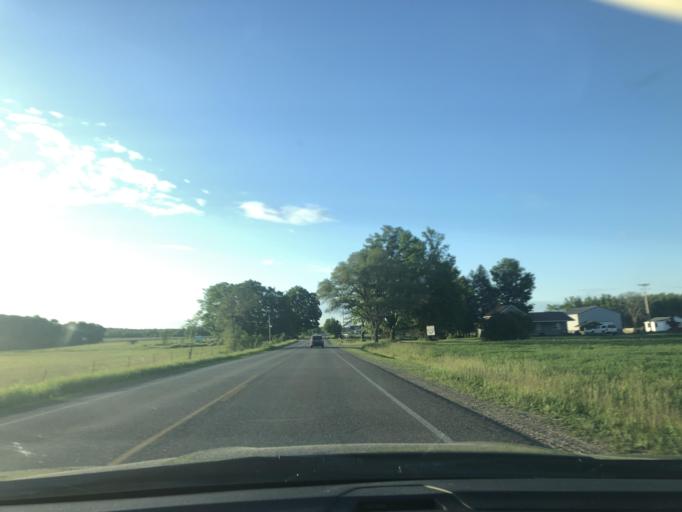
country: US
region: Michigan
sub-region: Missaukee County
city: Lake City
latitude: 44.4210
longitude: -85.0753
